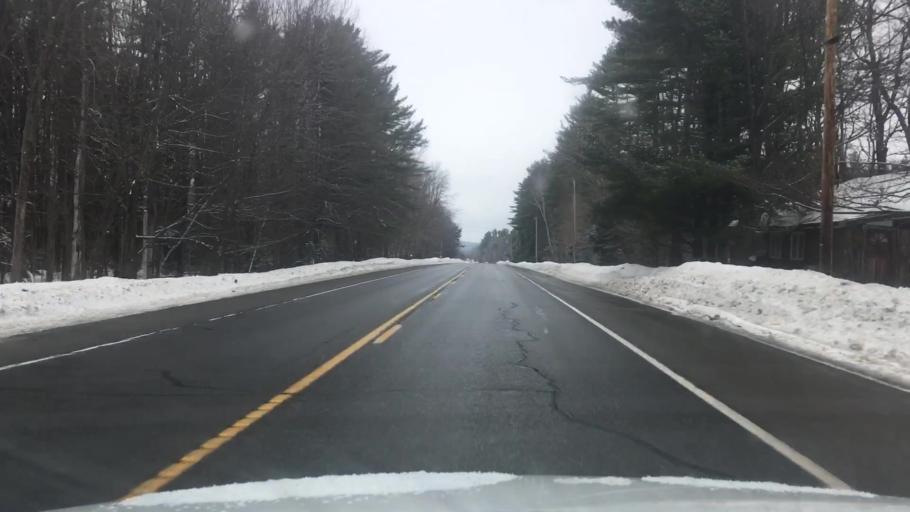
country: US
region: Maine
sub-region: Franklin County
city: New Sharon
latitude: 44.6593
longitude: -69.9558
